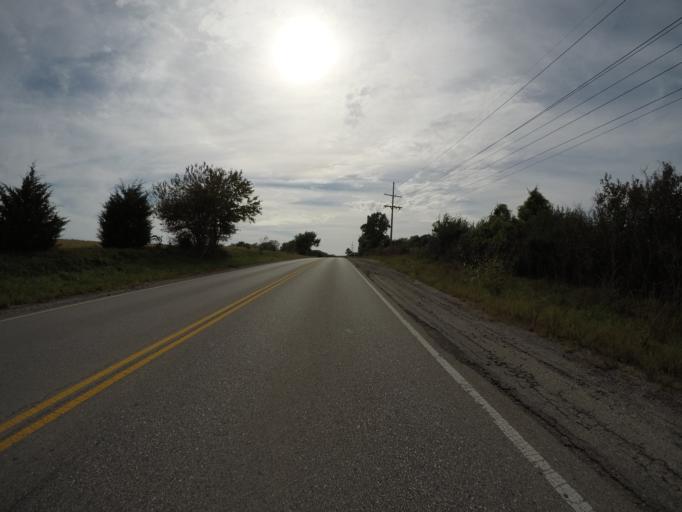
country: US
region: Kansas
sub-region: Johnson County
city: Olathe
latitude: 38.8630
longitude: -94.8479
